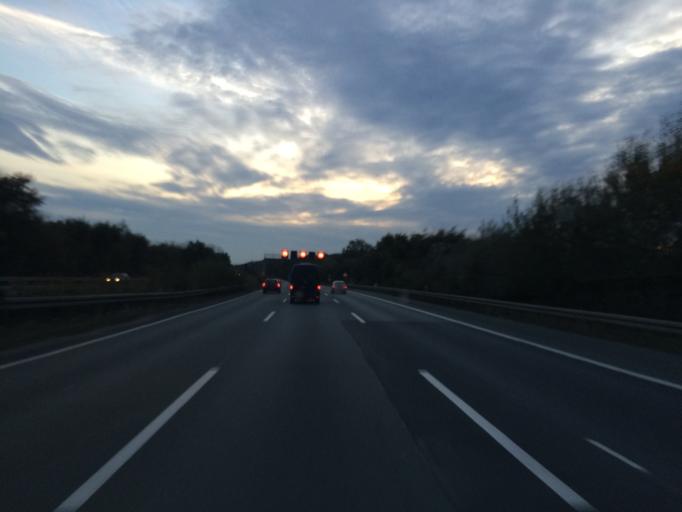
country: DE
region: Lower Saxony
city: Garbsen
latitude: 52.4173
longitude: 9.5250
